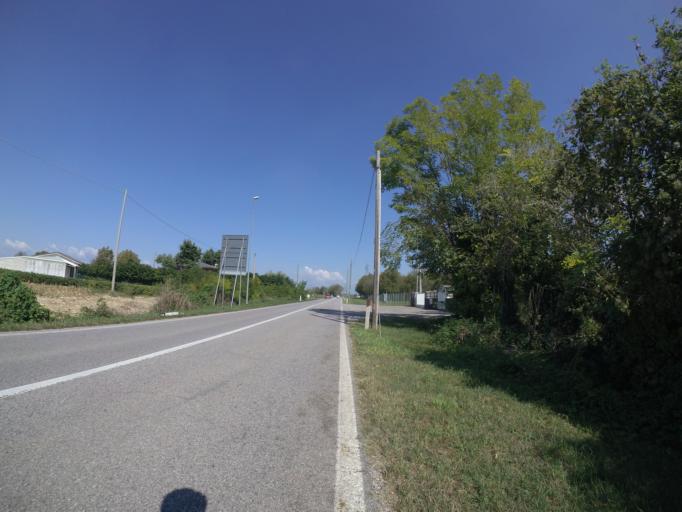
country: IT
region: Friuli Venezia Giulia
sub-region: Provincia di Udine
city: Codroipo
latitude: 45.9780
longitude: 12.9911
